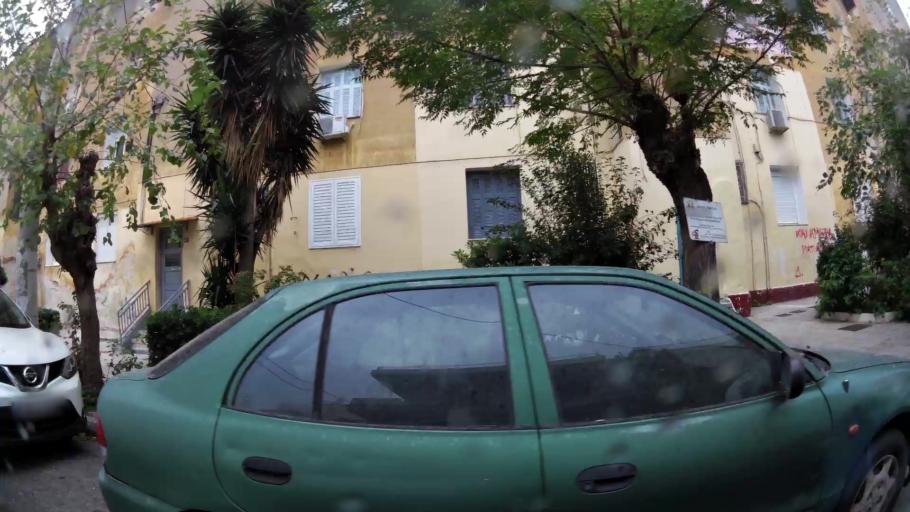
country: GR
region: Attica
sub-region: Nomos Piraios
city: Nikaia
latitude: 37.9612
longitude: 23.6506
